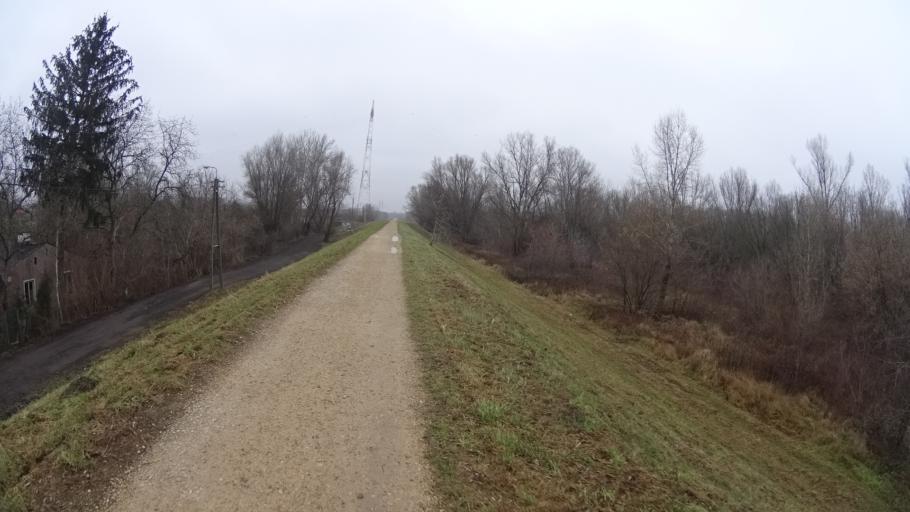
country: PL
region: Masovian Voivodeship
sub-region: Warszawa
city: Wilanow
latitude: 52.1954
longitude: 21.1006
